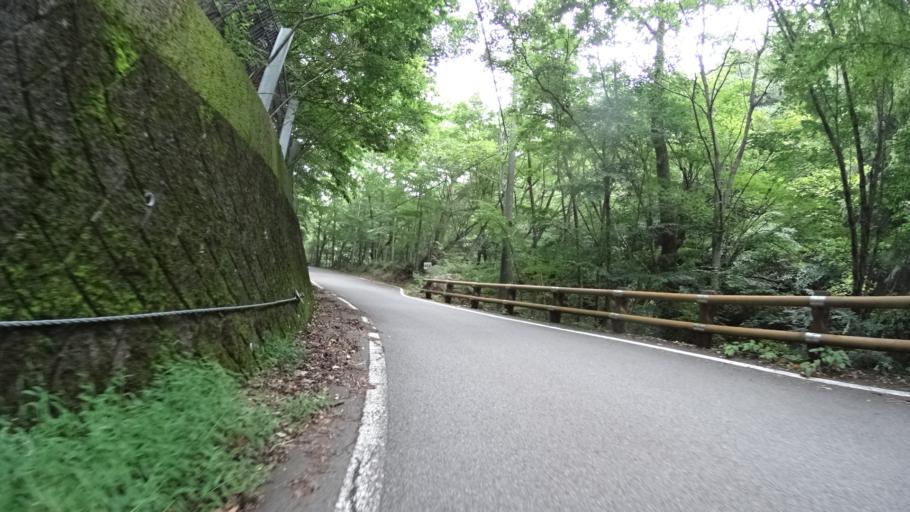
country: JP
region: Yamanashi
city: Kofu-shi
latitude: 35.8582
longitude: 138.5646
